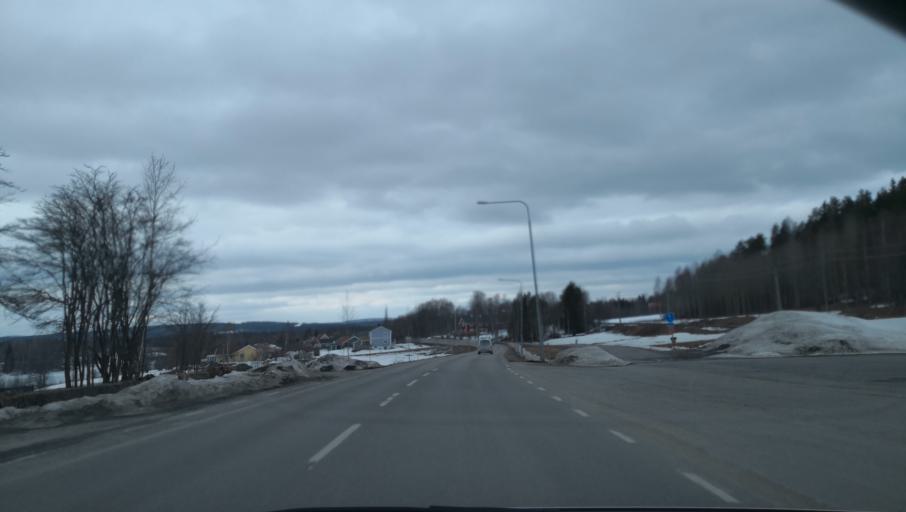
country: SE
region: Vaesterbotten
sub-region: Vannas Kommun
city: Vannasby
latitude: 63.9161
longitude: 19.8035
